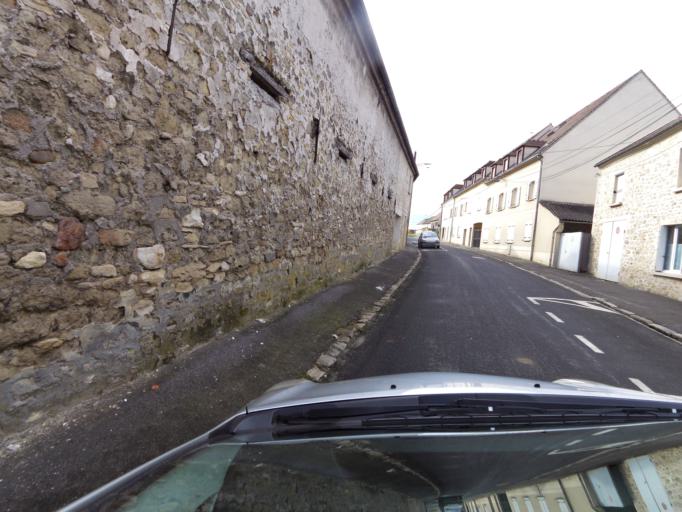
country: FR
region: Picardie
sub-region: Departement de l'Oise
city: Ver-sur-Launette
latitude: 49.1030
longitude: 2.6857
